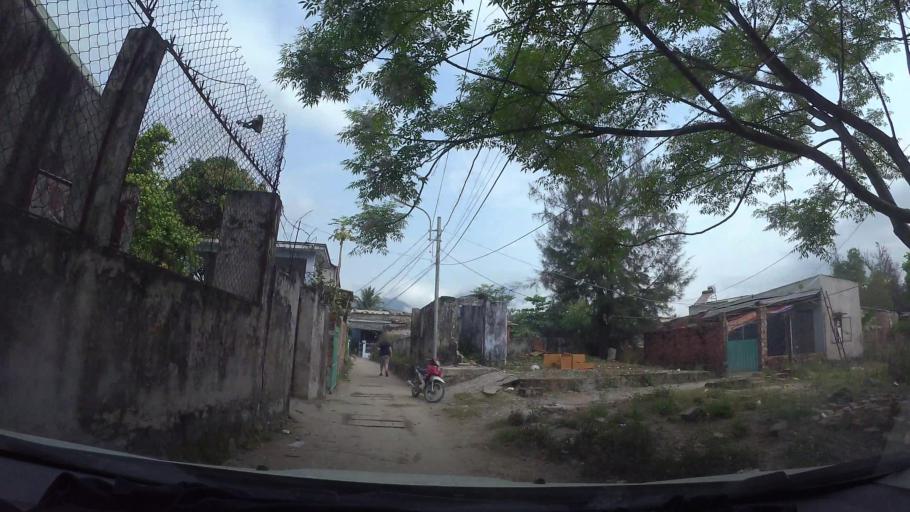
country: VN
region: Da Nang
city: Lien Chieu
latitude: 16.1235
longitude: 108.1228
